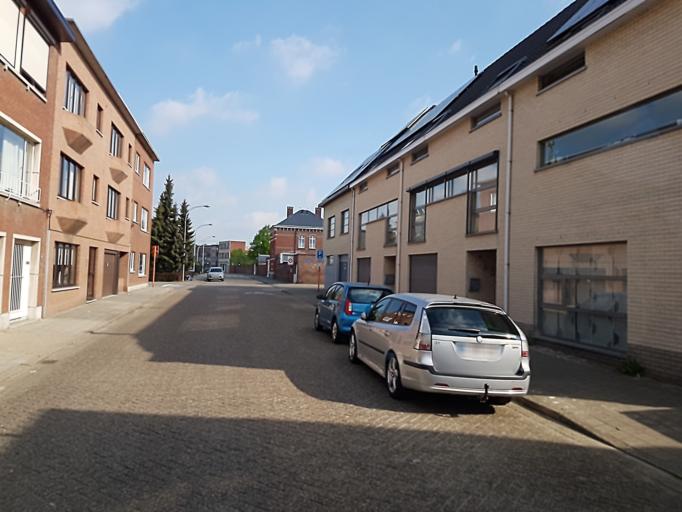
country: BE
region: Flanders
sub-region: Provincie Antwerpen
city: Turnhout
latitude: 51.3173
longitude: 4.9572
